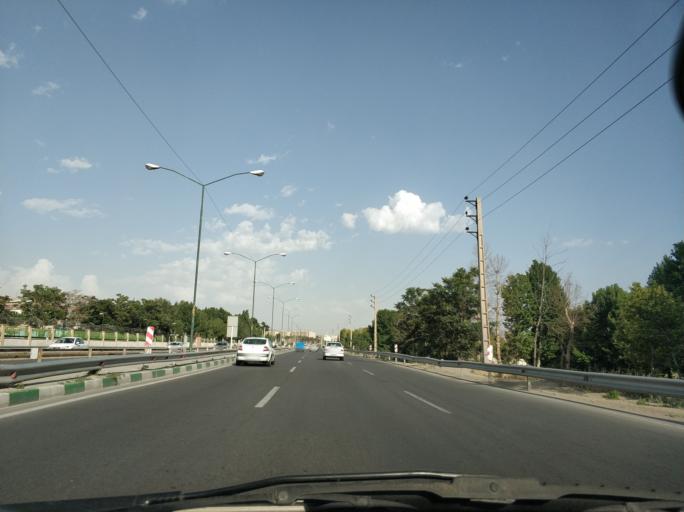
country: IR
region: Tehran
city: Tajrish
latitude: 35.7513
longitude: 51.5805
